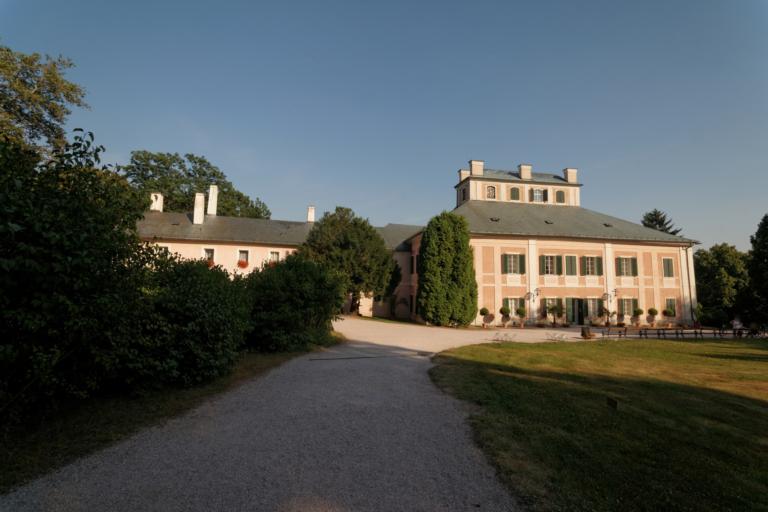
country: CZ
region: Kralovehradecky
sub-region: Okres Nachod
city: Ceska Skalice
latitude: 50.4153
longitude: 16.0522
